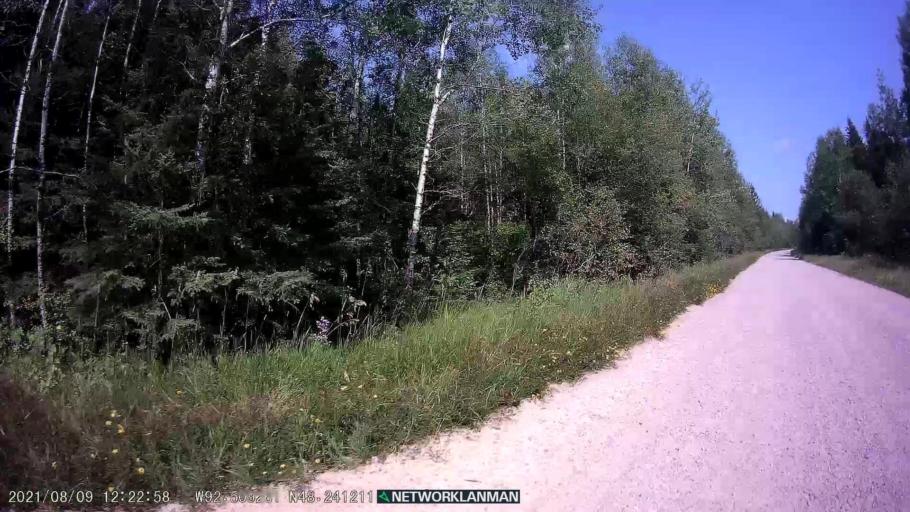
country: US
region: Minnesota
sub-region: Saint Louis County
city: Parkville
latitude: 48.2412
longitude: -92.5094
